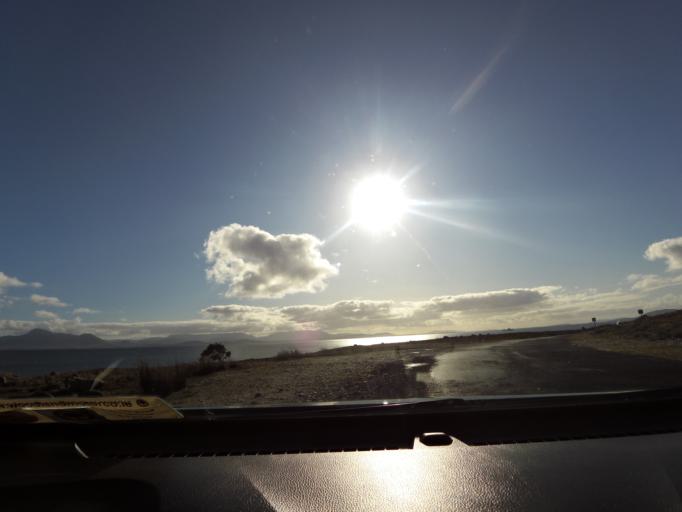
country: IE
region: Connaught
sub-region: Maigh Eo
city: Westport
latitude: 53.8787
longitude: -9.8165
